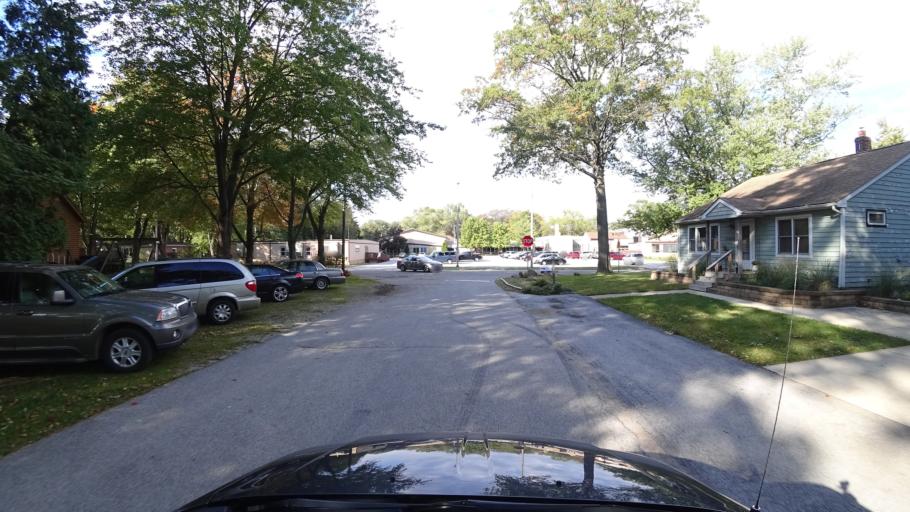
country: US
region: Indiana
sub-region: LaPorte County
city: Trail Creek
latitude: 41.7047
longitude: -86.8722
